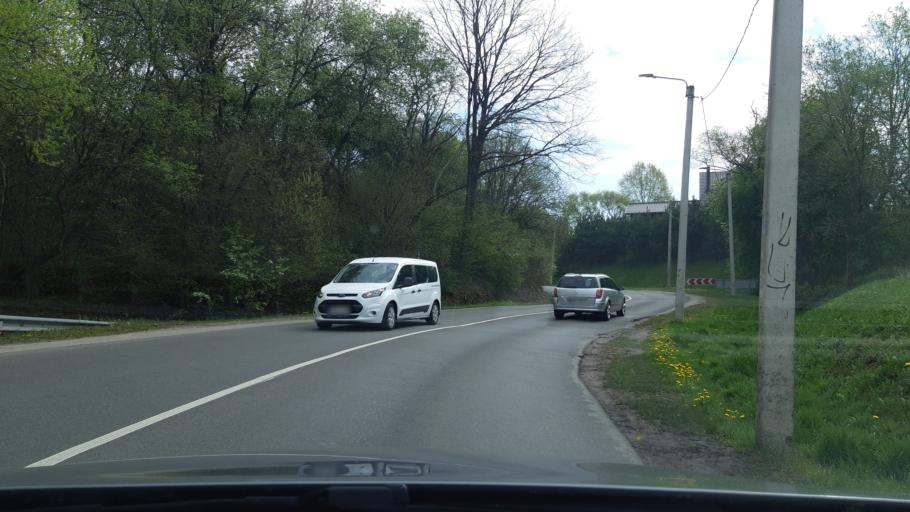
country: LT
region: Kauno apskritis
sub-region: Kaunas
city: Silainiai
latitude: 54.9237
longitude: 23.8653
